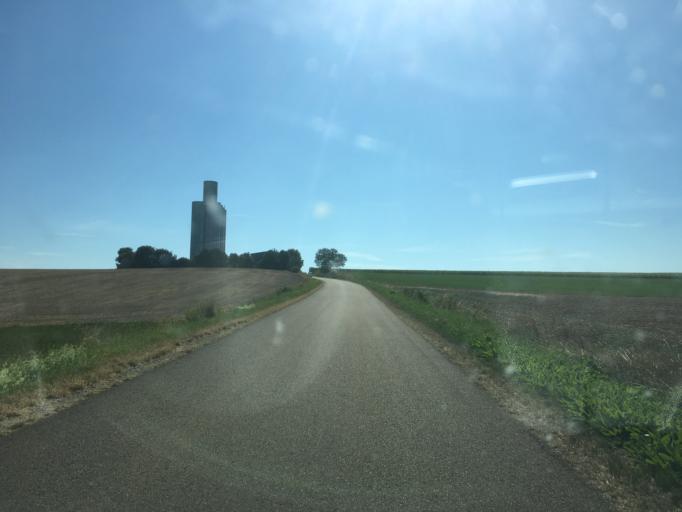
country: FR
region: Bourgogne
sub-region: Departement de l'Yonne
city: Fleury-la-Vallee
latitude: 47.9145
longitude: 3.4236
